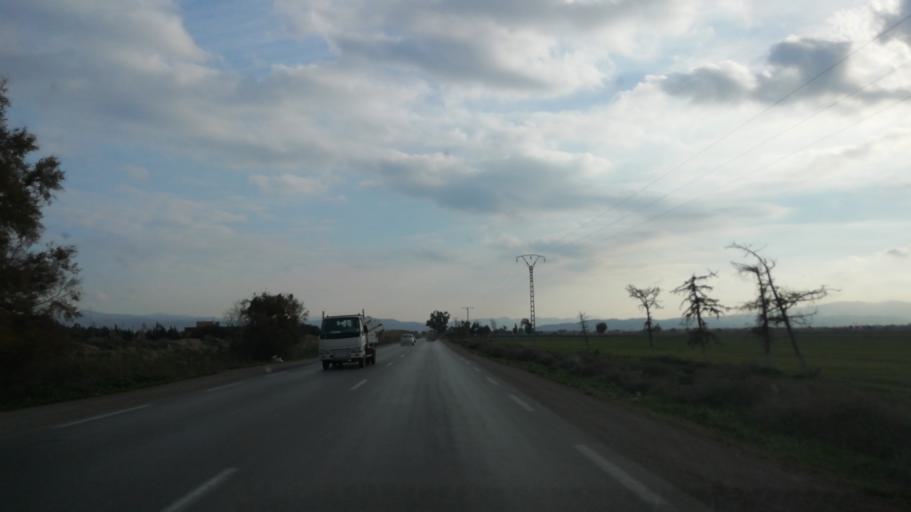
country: DZ
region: Mascara
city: Mascara
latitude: 35.6497
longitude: 0.0596
